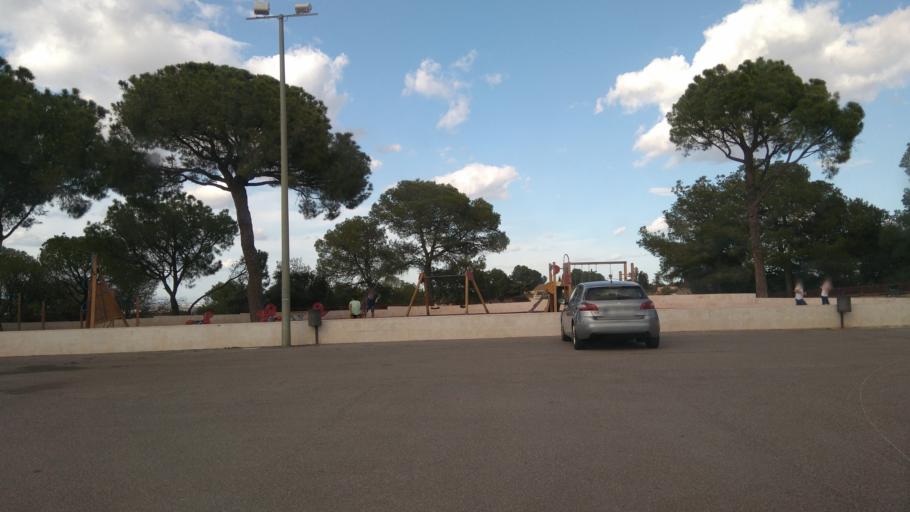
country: ES
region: Valencia
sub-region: Provincia de Valencia
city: Alzira
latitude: 39.1527
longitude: -0.4193
